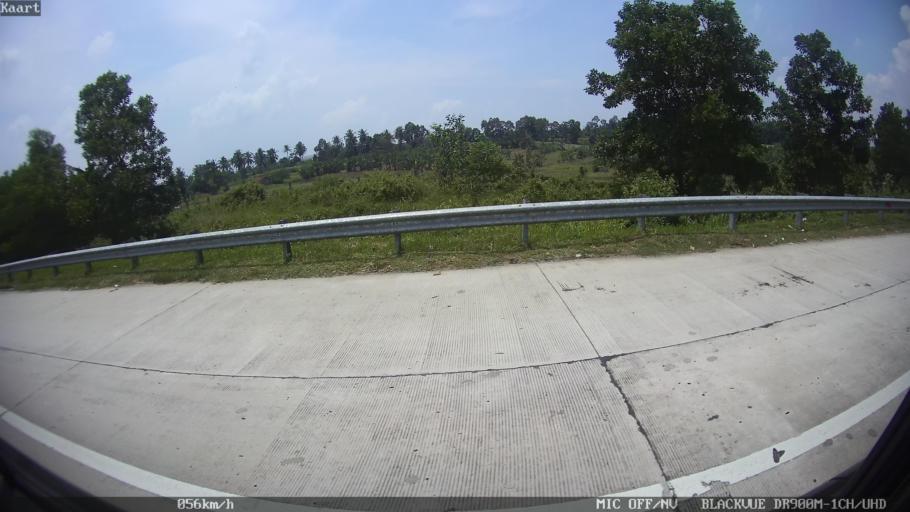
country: ID
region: Lampung
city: Natar
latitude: -5.2751
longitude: 105.2128
